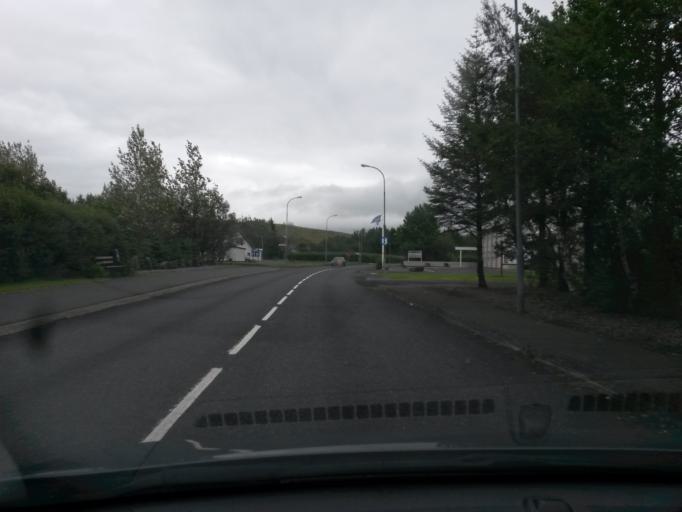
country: IS
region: South
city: Vestmannaeyjar
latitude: 63.7507
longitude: -20.2256
